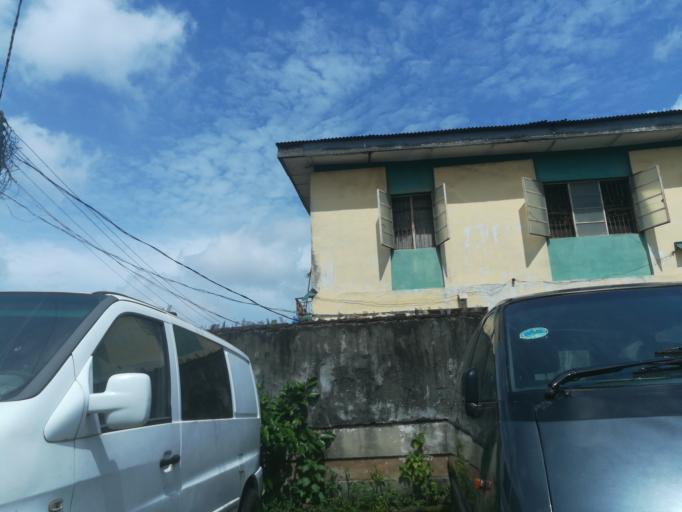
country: NG
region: Lagos
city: Somolu
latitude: 6.5270
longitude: 3.3802
